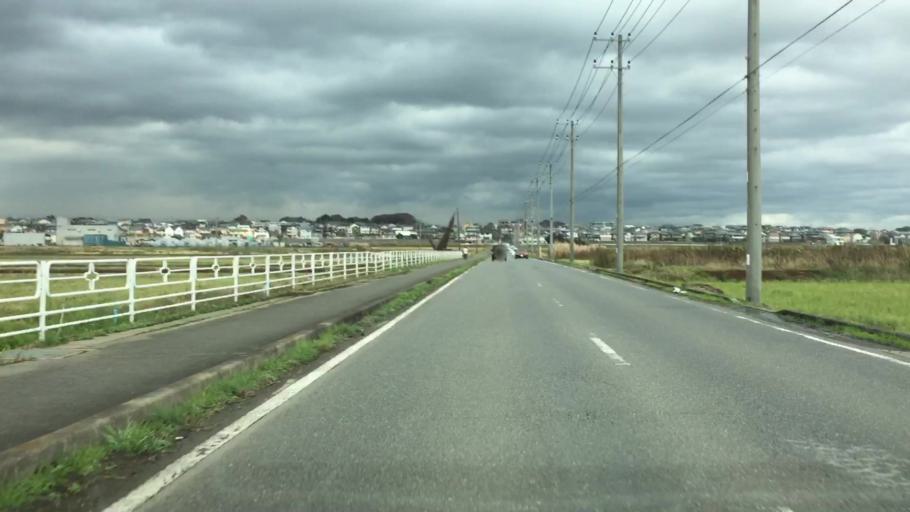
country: JP
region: Ibaraki
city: Toride
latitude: 35.8526
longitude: 140.1006
